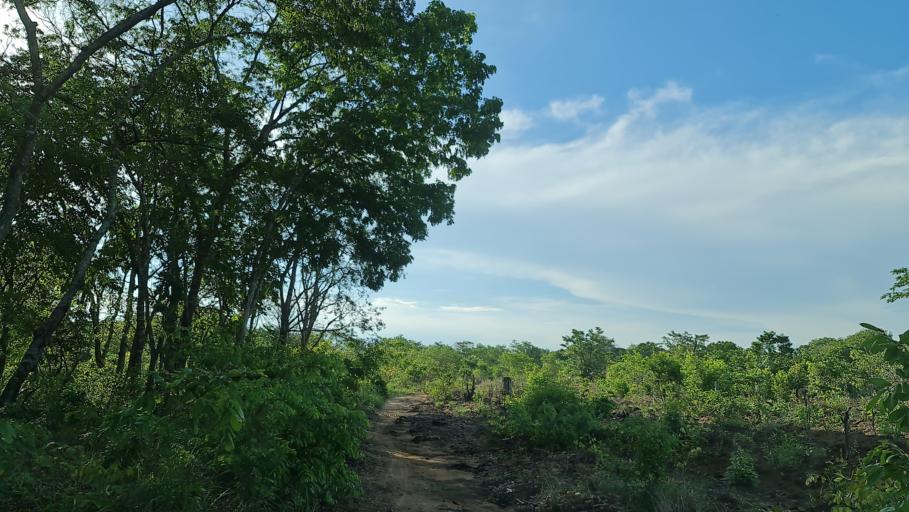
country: MZ
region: Zambezia
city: Quelimane
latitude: -17.1929
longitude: 37.4149
